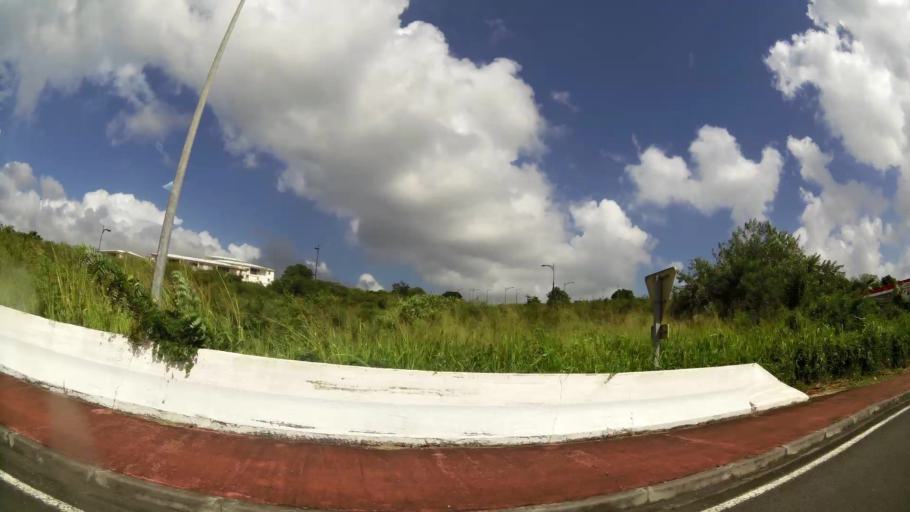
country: MQ
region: Martinique
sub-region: Martinique
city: Fort-de-France
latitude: 14.6365
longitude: -61.1357
